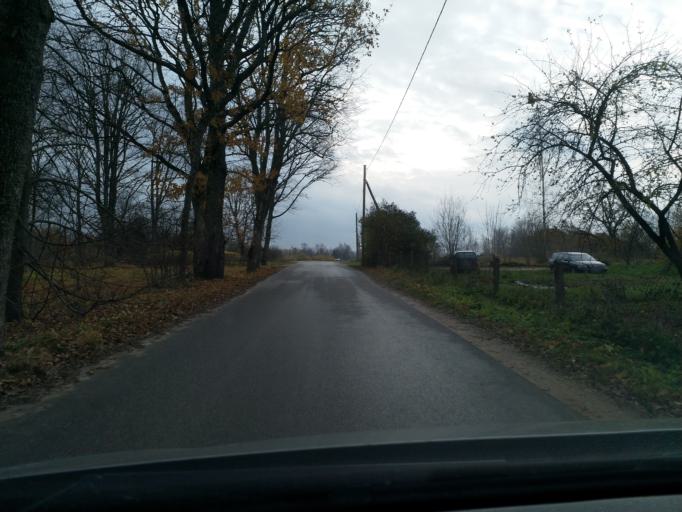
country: LV
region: Kuldigas Rajons
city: Kuldiga
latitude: 56.9809
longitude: 21.9751
